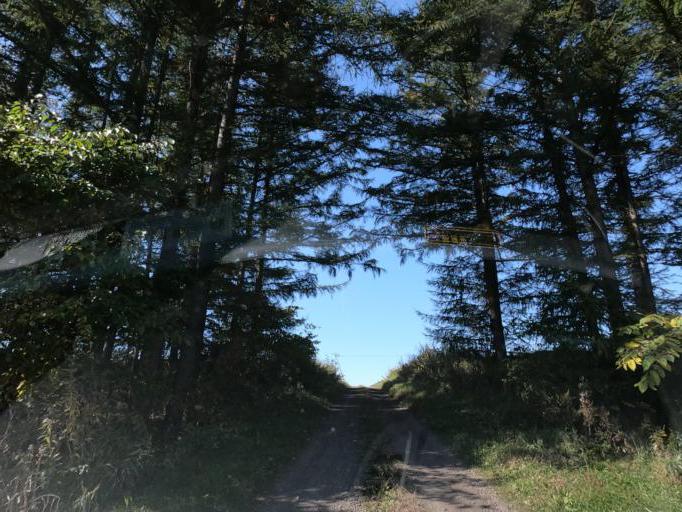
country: JP
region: Hokkaido
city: Otofuke
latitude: 43.0645
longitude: 143.2769
